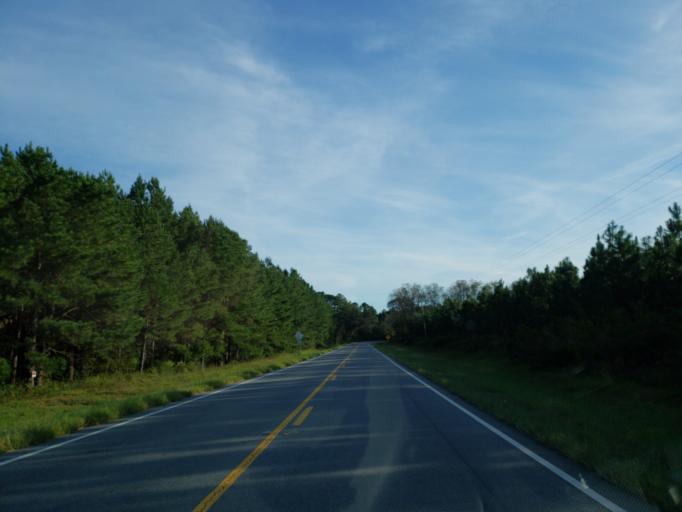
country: US
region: Georgia
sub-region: Crisp County
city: Cordele
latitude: 32.0118
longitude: -83.7350
